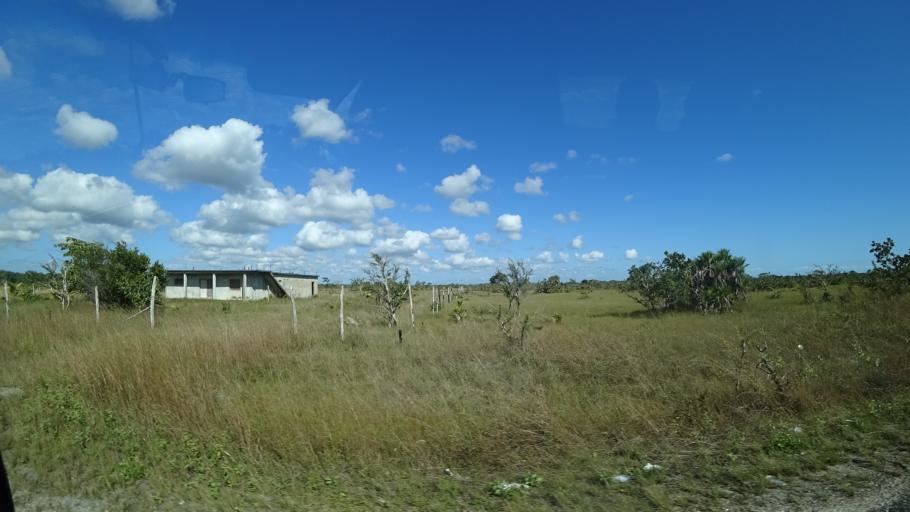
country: BZ
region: Belize
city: Belize City
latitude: 17.5806
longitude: -88.3790
